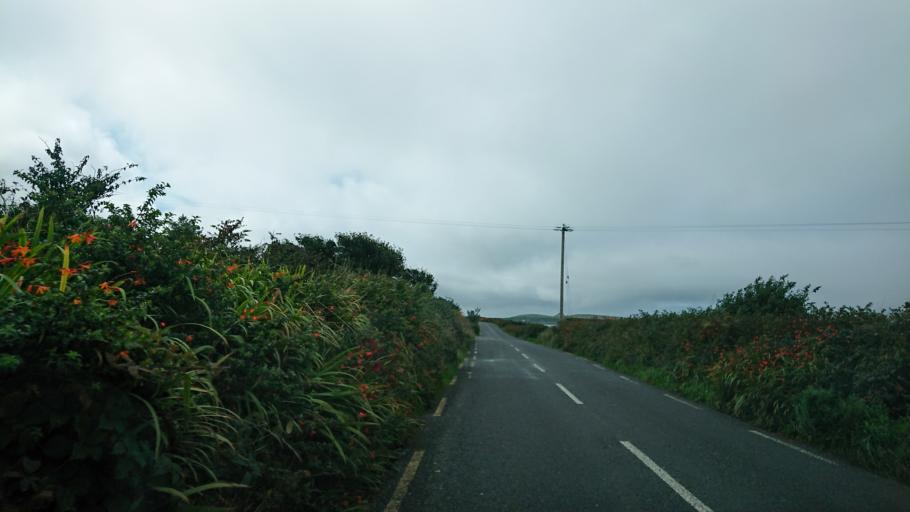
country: IE
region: Munster
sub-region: Ciarrai
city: Cahersiveen
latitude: 51.9330
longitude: -10.2603
